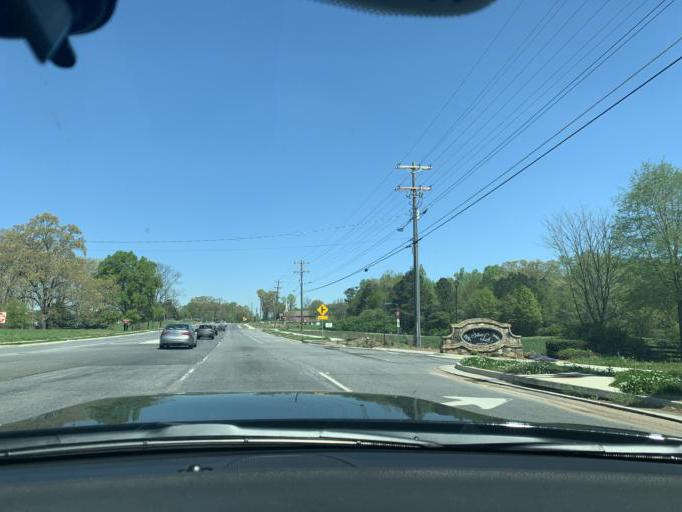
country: US
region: Georgia
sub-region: Forsyth County
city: Cumming
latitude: 34.1931
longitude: -84.1968
